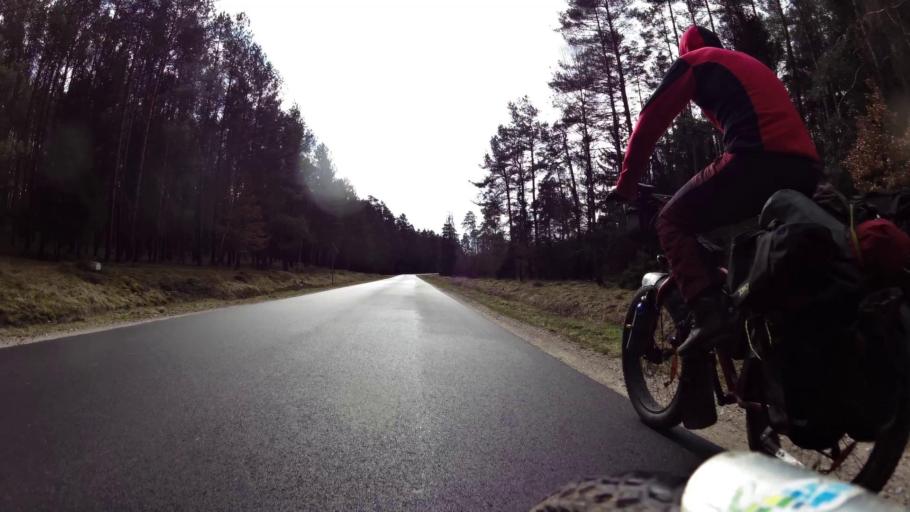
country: PL
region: Pomeranian Voivodeship
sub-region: Powiat bytowski
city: Kolczyglowy
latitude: 54.2044
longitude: 17.2352
